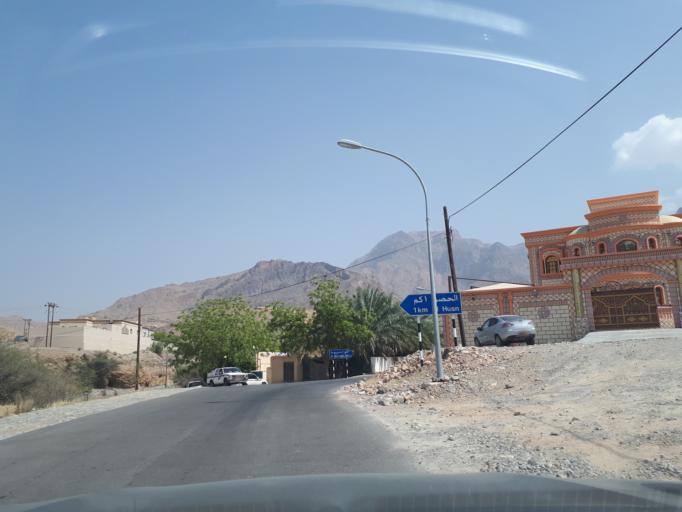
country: OM
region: Ash Sharqiyah
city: Ibra'
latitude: 23.0825
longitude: 58.8661
